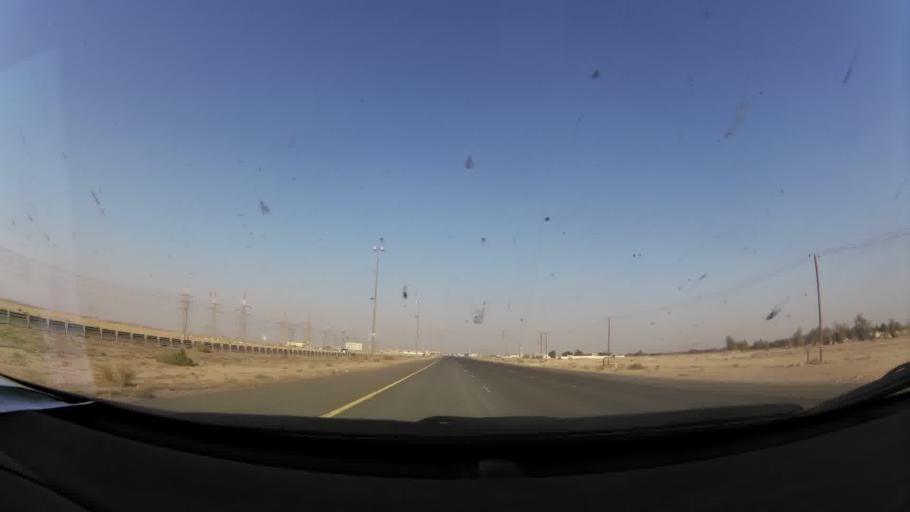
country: IQ
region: Basra Governorate
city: Umm Qasr
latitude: 30.0707
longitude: 47.6900
